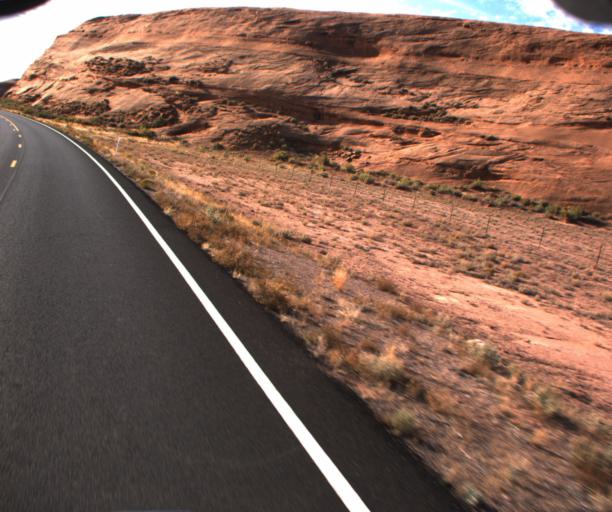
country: US
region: Arizona
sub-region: Apache County
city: Many Farms
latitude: 36.7725
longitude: -109.6612
